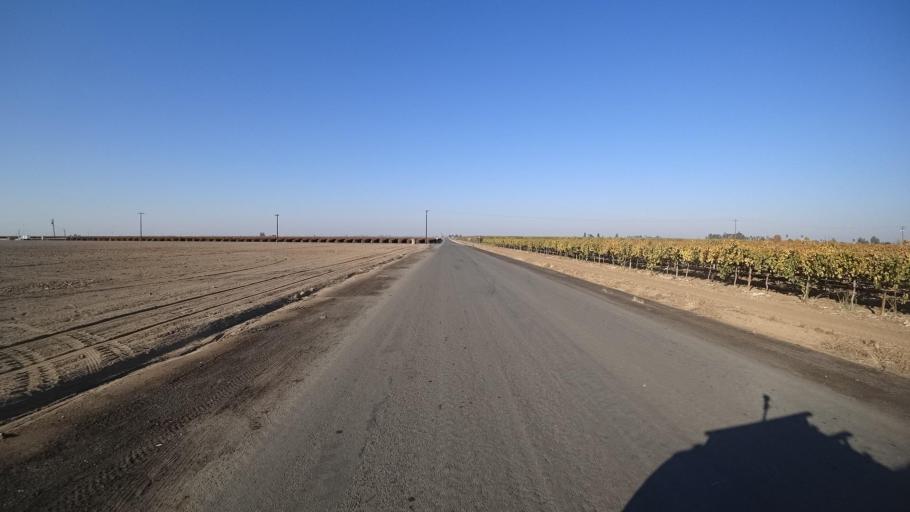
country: US
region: California
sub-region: Tulare County
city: Richgrove
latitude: 35.7676
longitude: -119.1666
